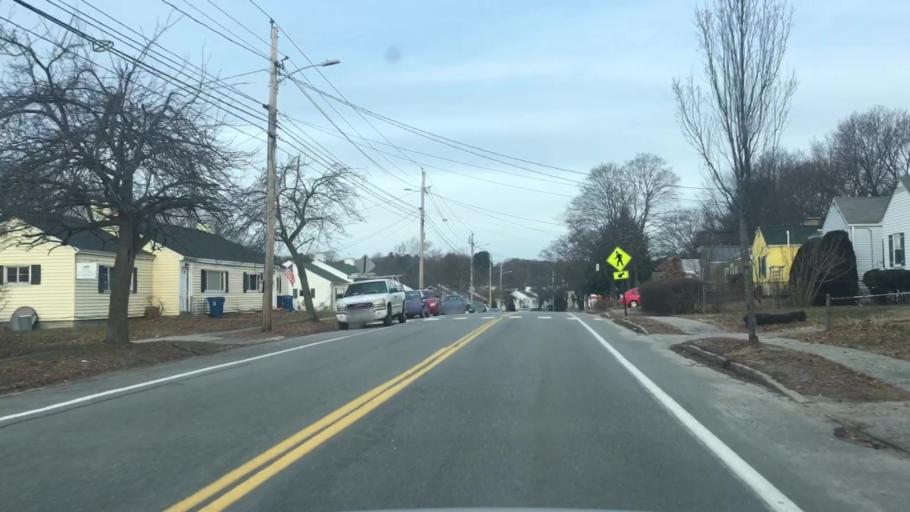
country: US
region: Maine
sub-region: Cumberland County
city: Portland
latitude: 43.6605
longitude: -70.2835
